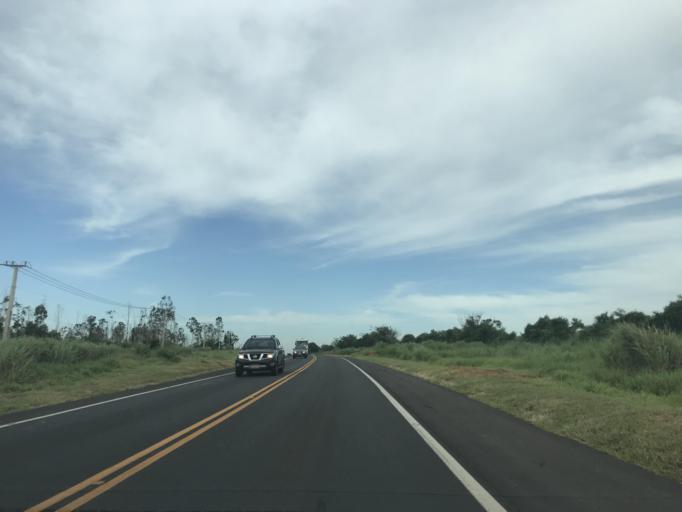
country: BR
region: Parana
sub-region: Paranavai
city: Paranavai
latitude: -23.0141
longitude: -52.5161
